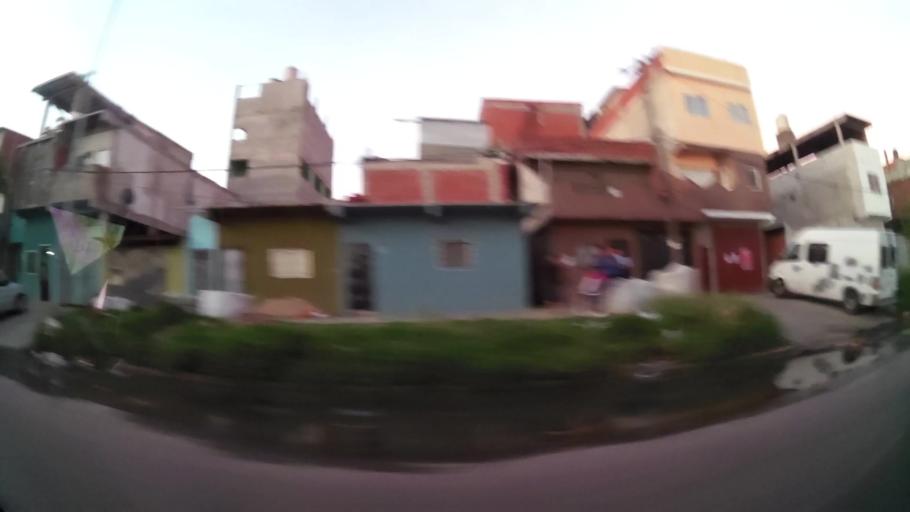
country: AR
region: Buenos Aires F.D.
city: Villa Lugano
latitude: -34.6506
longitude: -58.4372
